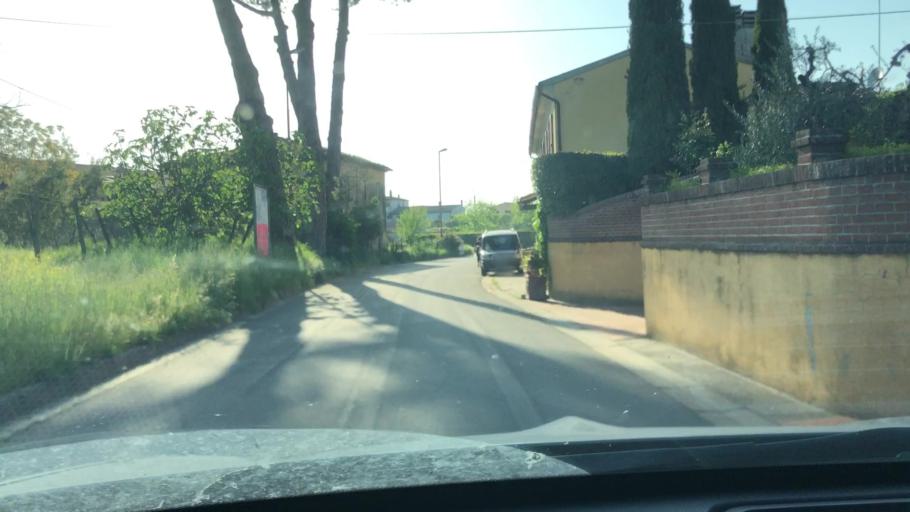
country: IT
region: Tuscany
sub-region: Province of Pisa
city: Cenaia
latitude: 43.5897
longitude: 10.5406
